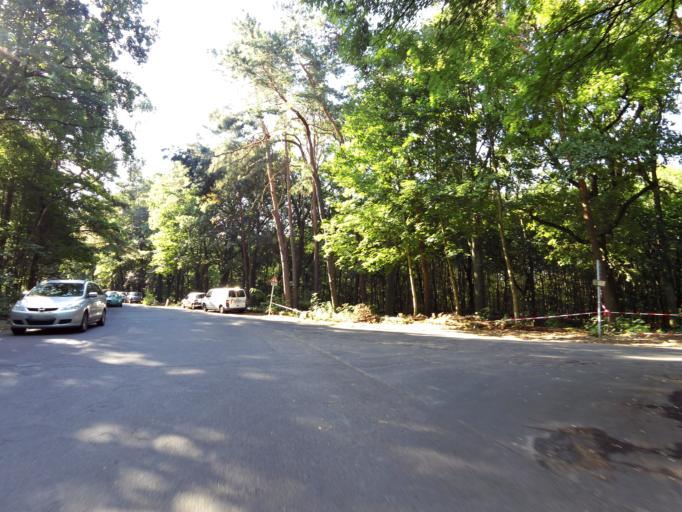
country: DE
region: Berlin
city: Nikolassee
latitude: 52.4374
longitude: 13.1817
